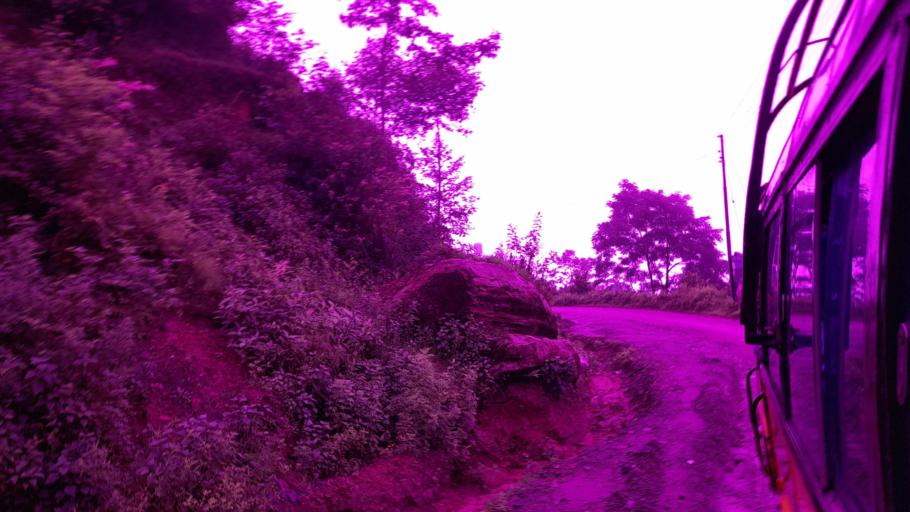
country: NP
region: Central Region
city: Kirtipur
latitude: 27.8198
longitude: 85.2258
